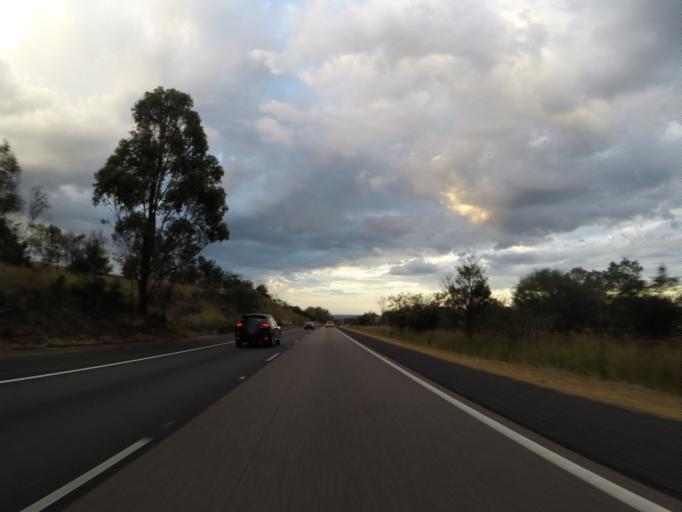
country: AU
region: New South Wales
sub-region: Wollondilly
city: Douglas Park
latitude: -34.2198
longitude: 150.6775
